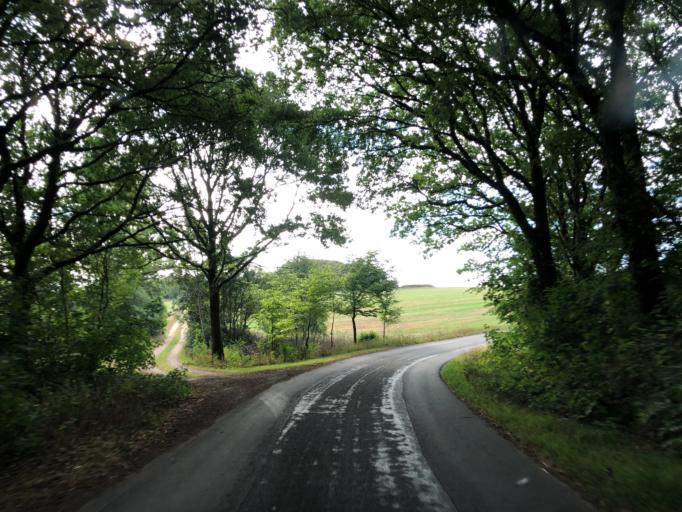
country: DK
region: Central Jutland
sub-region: Ringkobing-Skjern Kommune
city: Skjern
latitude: 56.0478
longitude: 8.4109
